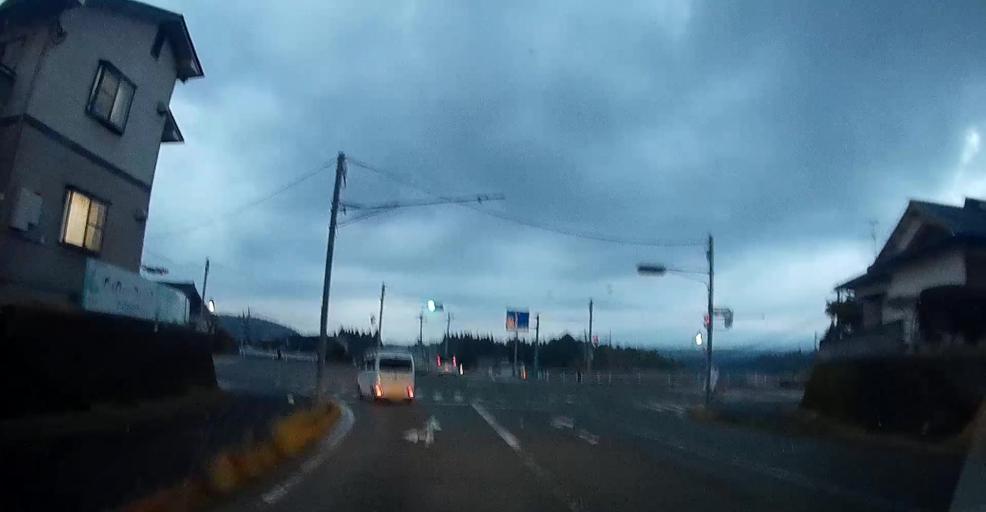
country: JP
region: Kumamoto
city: Ozu
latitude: 32.8396
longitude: 130.9162
